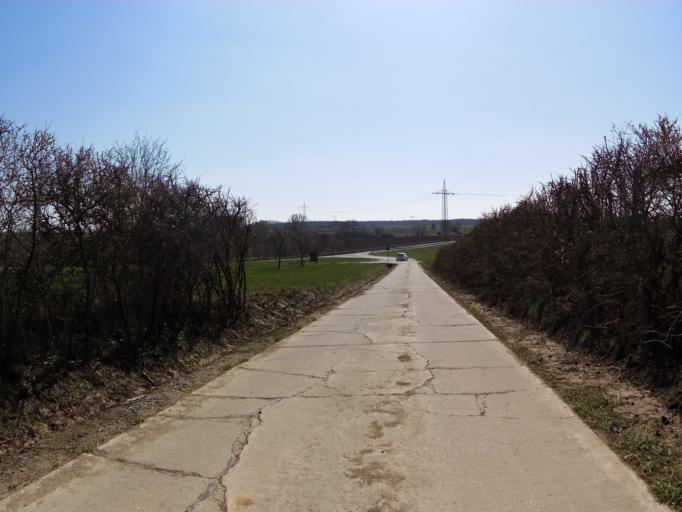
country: DE
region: Bavaria
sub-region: Regierungsbezirk Unterfranken
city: Biebelried
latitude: 49.7351
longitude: 10.0938
